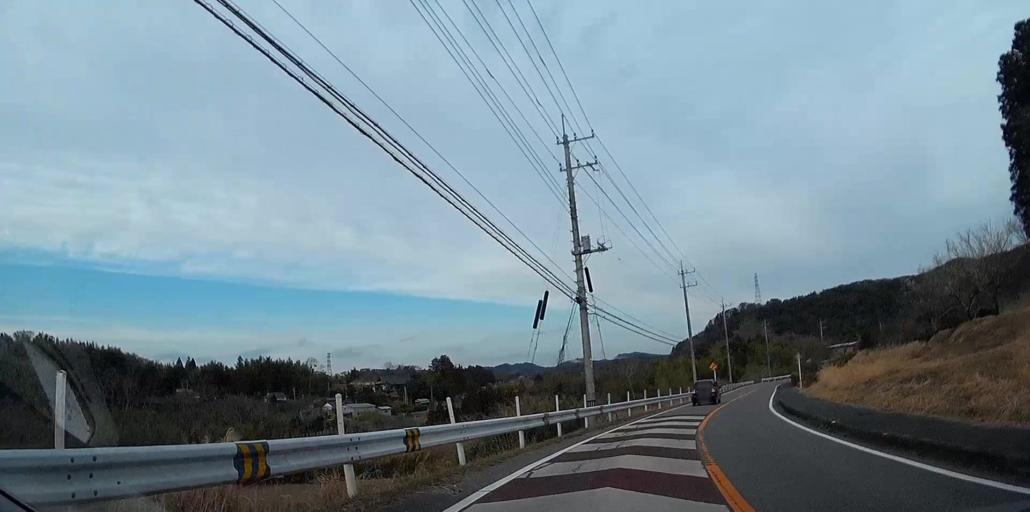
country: JP
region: Chiba
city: Kisarazu
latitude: 35.2677
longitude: 140.0576
